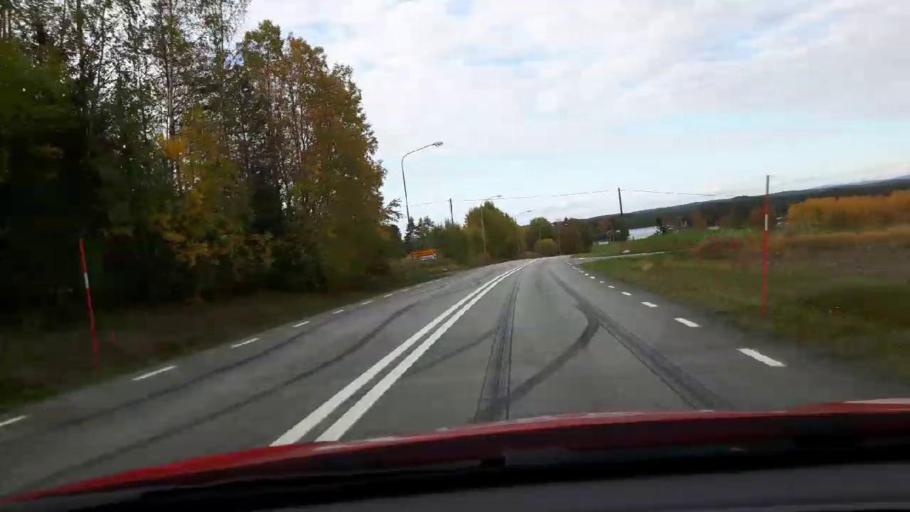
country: SE
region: Jaemtland
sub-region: Krokoms Kommun
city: Valla
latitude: 63.2404
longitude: 14.0019
